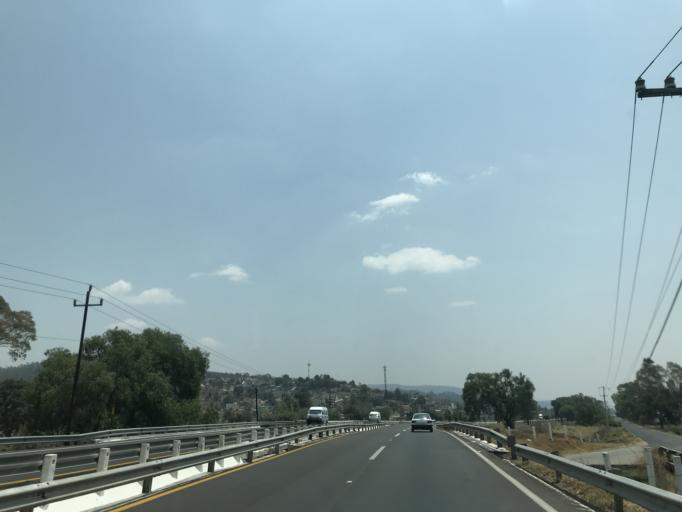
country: MX
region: Tlaxcala
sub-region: Ixtacuixtla de Mariano Matamoros
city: Santa Justina Ecatepec
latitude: 19.3290
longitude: -98.3568
